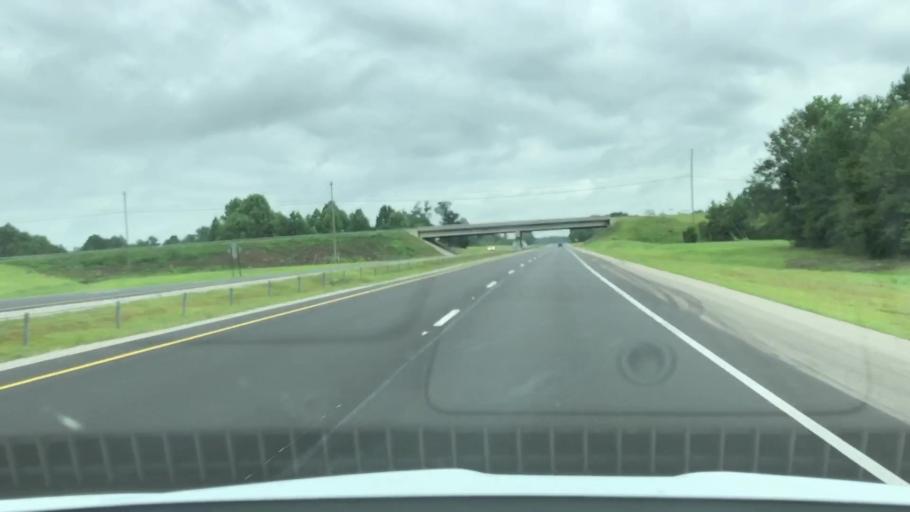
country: US
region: North Carolina
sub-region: Wilson County
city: Lucama
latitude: 35.6182
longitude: -77.9784
